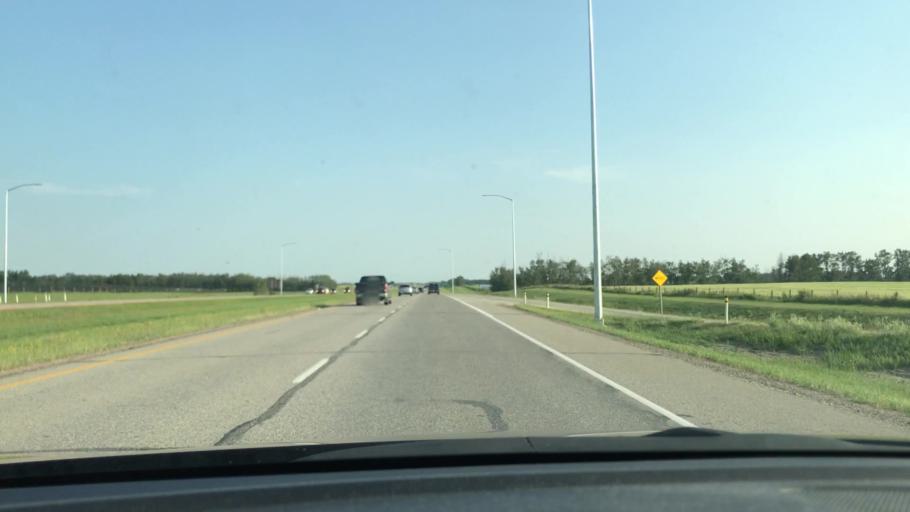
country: CA
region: Alberta
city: Millet
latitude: 53.0882
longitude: -113.5984
